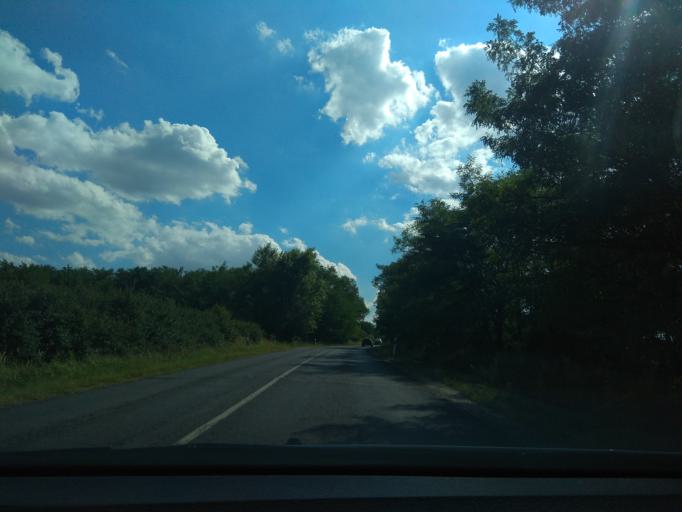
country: HU
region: Borsod-Abauj-Zemplen
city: Malyi
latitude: 48.0472
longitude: 20.7931
